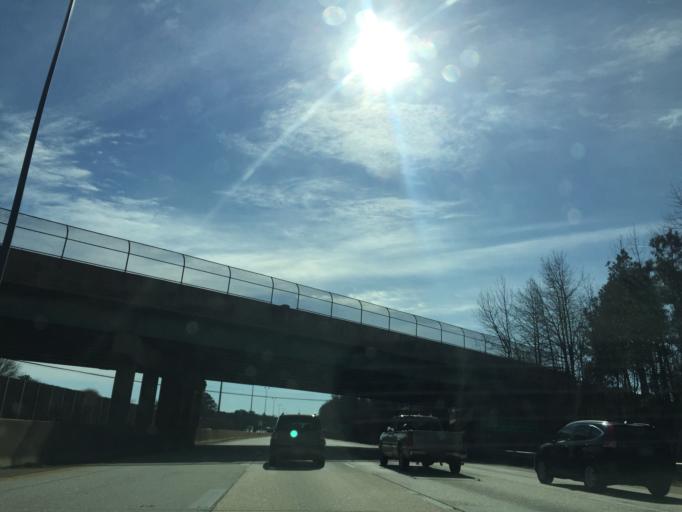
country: US
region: Virginia
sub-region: City of Newport News
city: Newport News
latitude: 37.0662
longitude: -76.4283
